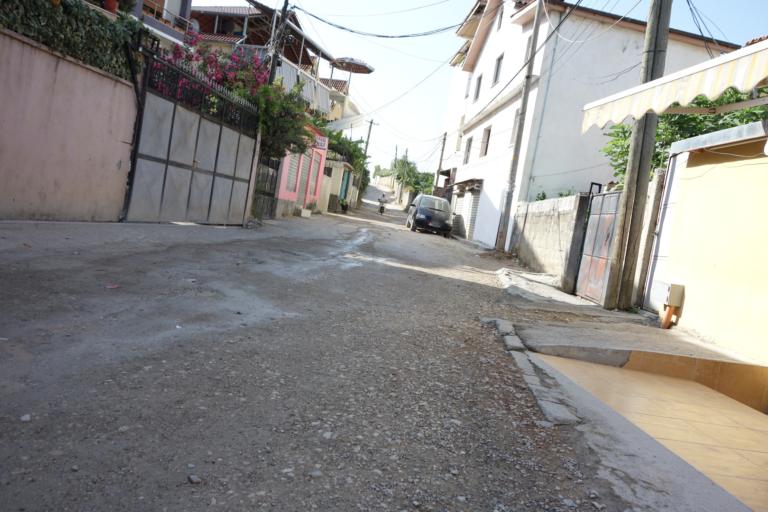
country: AL
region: Tirane
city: Tirana
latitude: 41.3359
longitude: 19.8443
